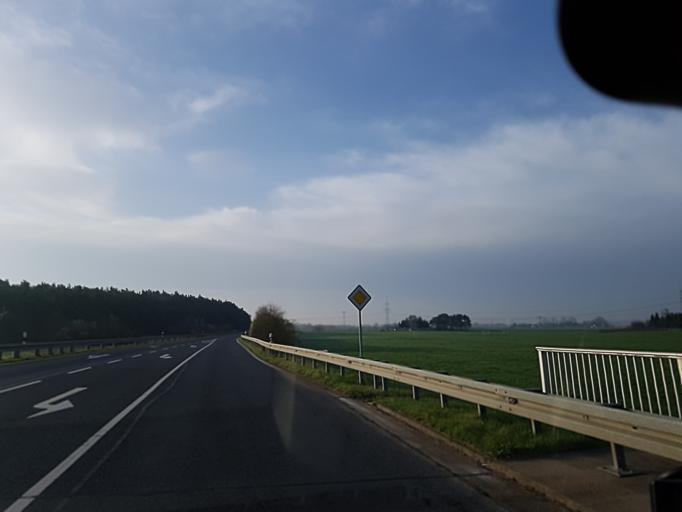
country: DE
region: Saxony
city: Riesa
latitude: 51.3458
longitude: 13.2965
